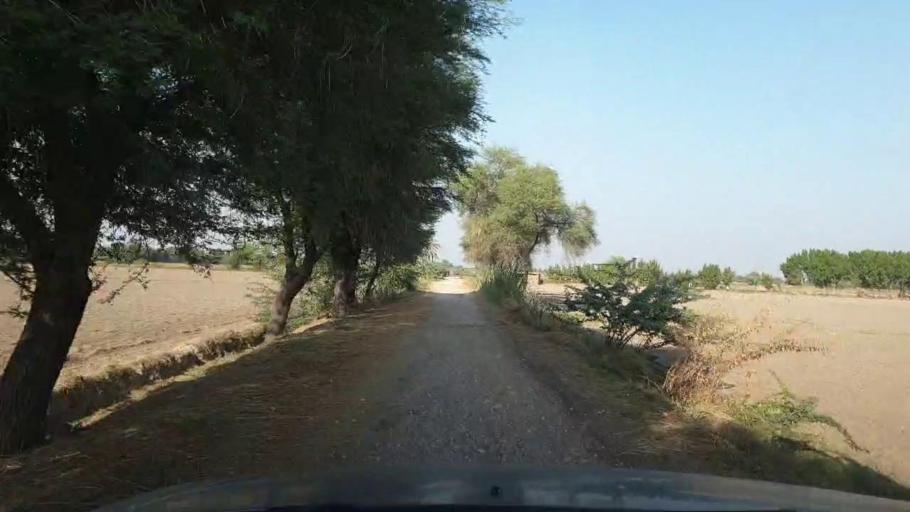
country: PK
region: Sindh
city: Tando Muhammad Khan
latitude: 25.0918
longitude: 68.5750
